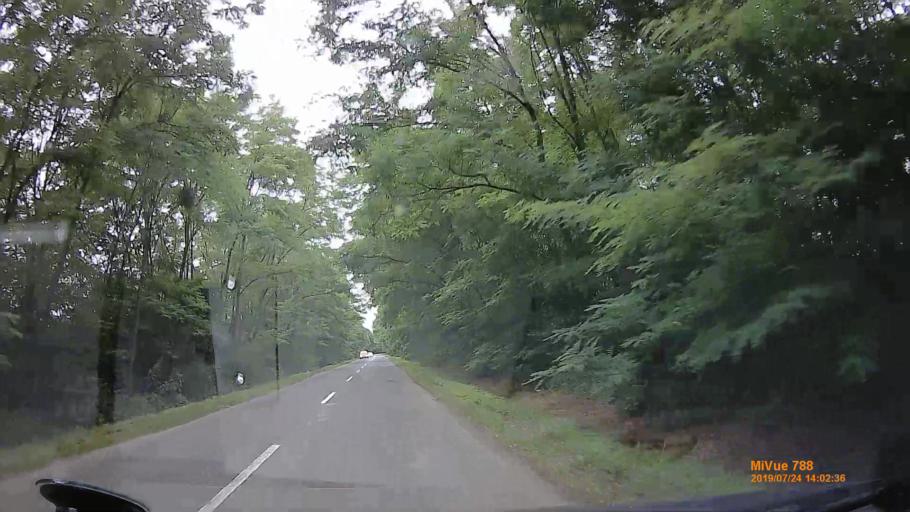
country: HU
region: Szabolcs-Szatmar-Bereg
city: Aranyosapati
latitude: 48.2693
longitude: 22.2865
